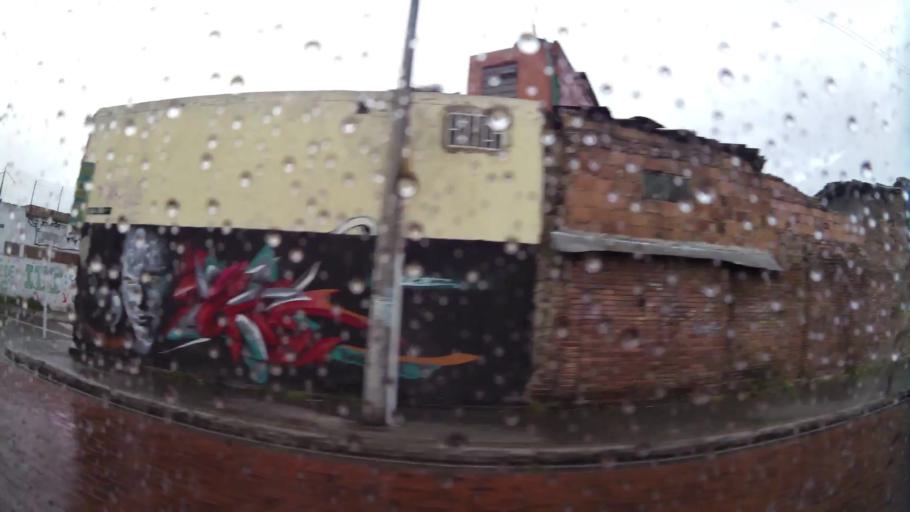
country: CO
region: Bogota D.C.
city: Bogota
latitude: 4.5864
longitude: -74.1422
